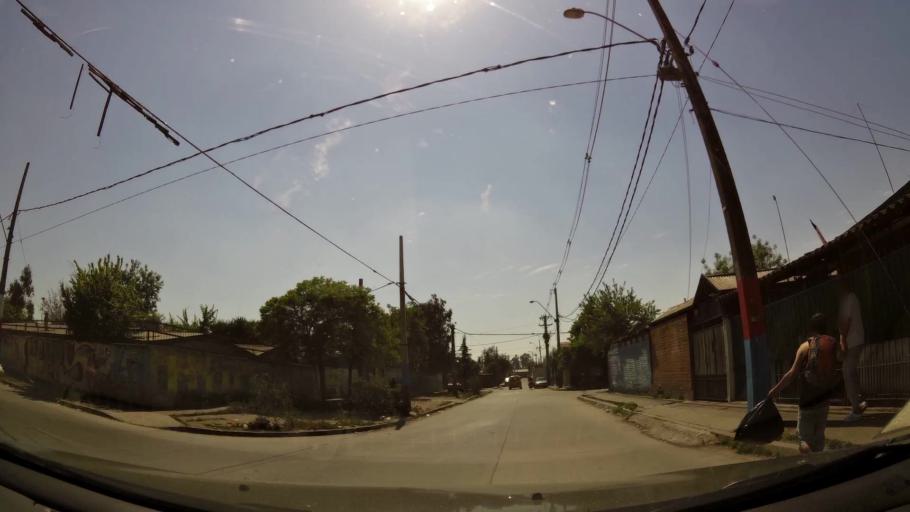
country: CL
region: Santiago Metropolitan
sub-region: Provincia de Santiago
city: La Pintana
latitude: -33.5915
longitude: -70.6227
